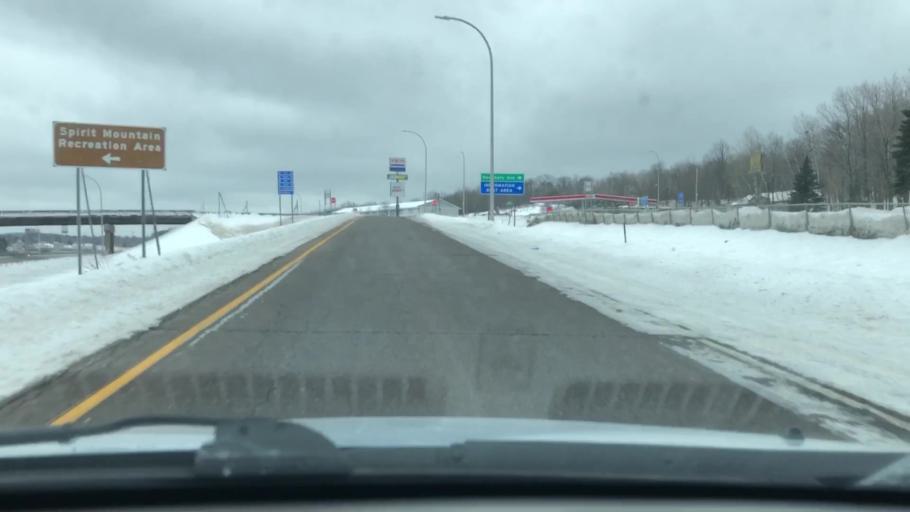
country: US
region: Minnesota
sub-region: Saint Louis County
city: Proctor
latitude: 46.7264
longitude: -92.2153
